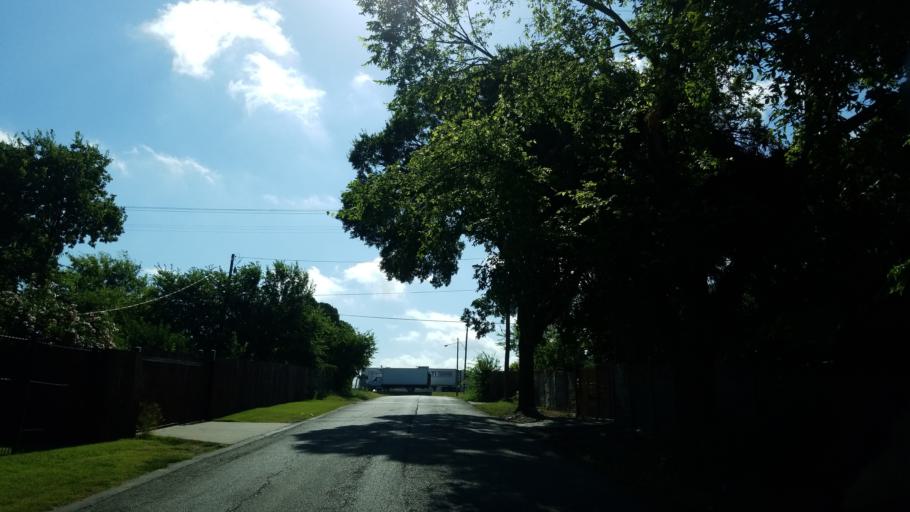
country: US
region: Texas
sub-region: Dallas County
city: Dallas
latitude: 32.7167
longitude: -96.8069
